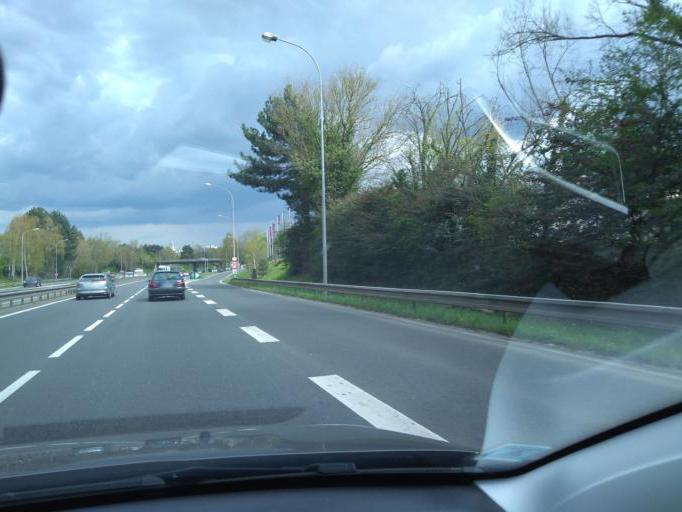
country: FR
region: Pays de la Loire
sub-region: Departement de Maine-et-Loire
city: Avrille
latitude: 47.4694
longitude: -0.5948
